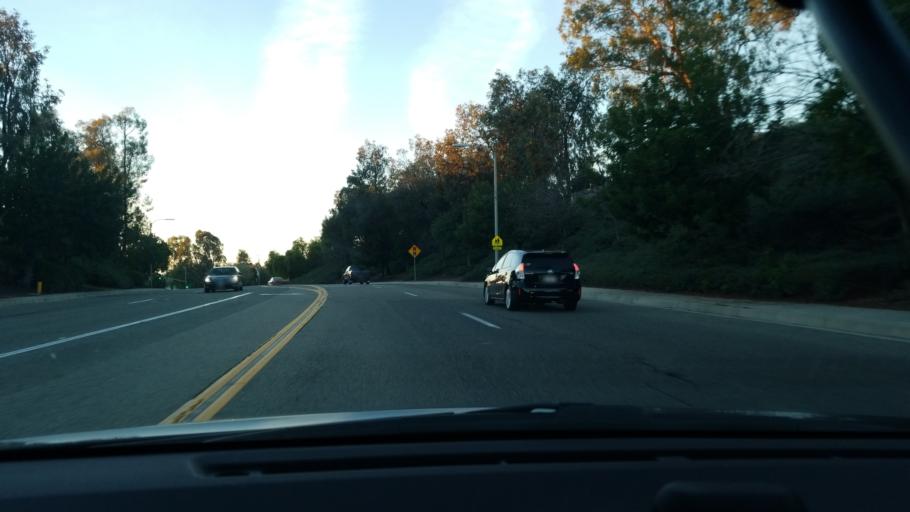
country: US
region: California
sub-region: Riverside County
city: Temecula
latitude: 33.5109
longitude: -117.0978
